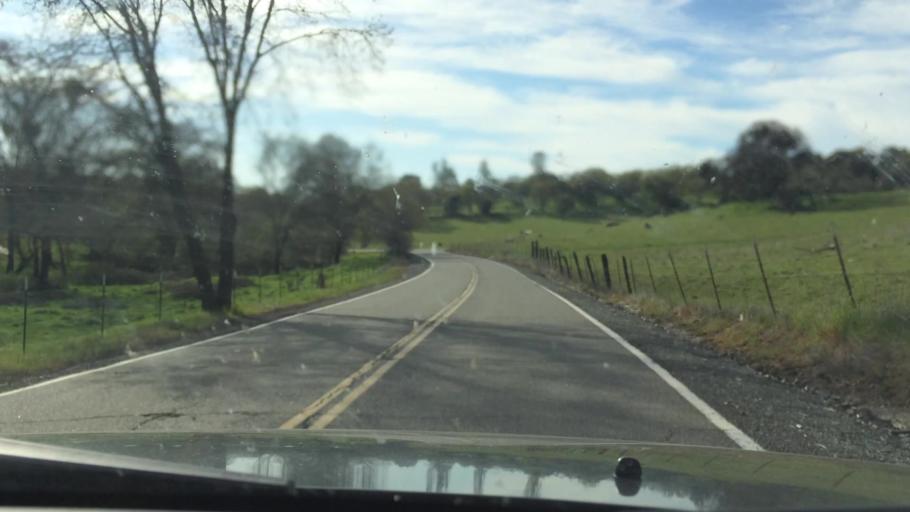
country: US
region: California
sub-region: Amador County
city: Plymouth
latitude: 38.4805
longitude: -120.8629
